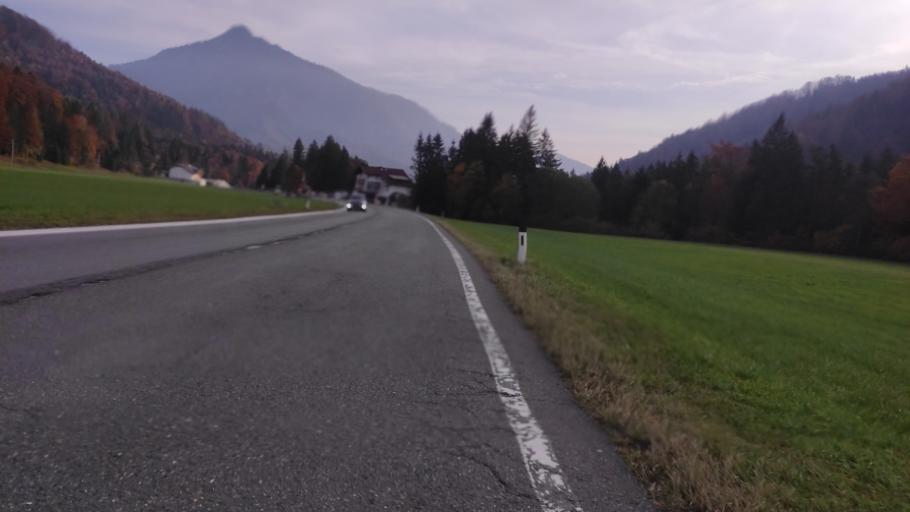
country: AT
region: Salzburg
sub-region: Politischer Bezirk Salzburg-Umgebung
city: Ebenau
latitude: 47.7843
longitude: 13.1787
